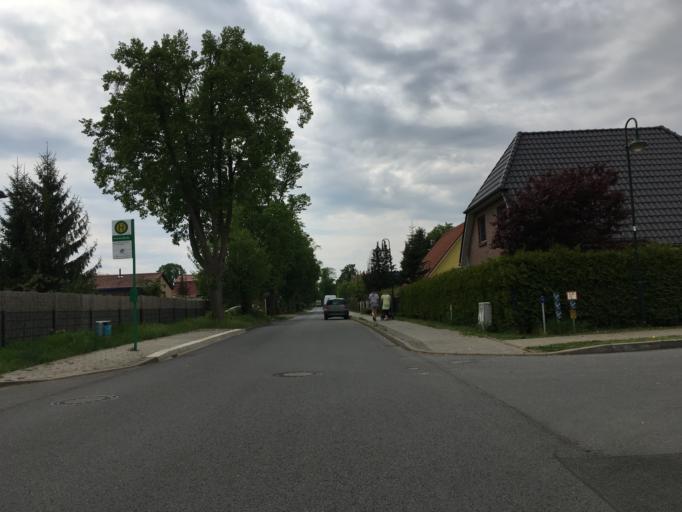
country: DE
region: Berlin
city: Buch
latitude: 52.6254
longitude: 13.5239
